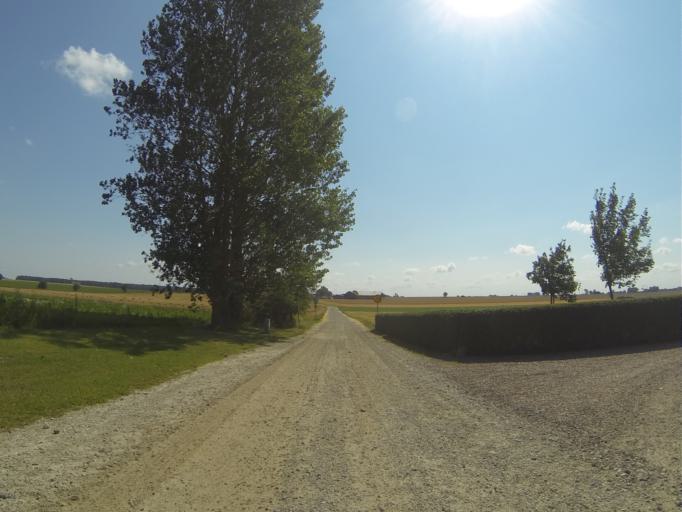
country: SE
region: Skane
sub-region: Lunds Kommun
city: Lund
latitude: 55.7320
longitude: 13.2522
